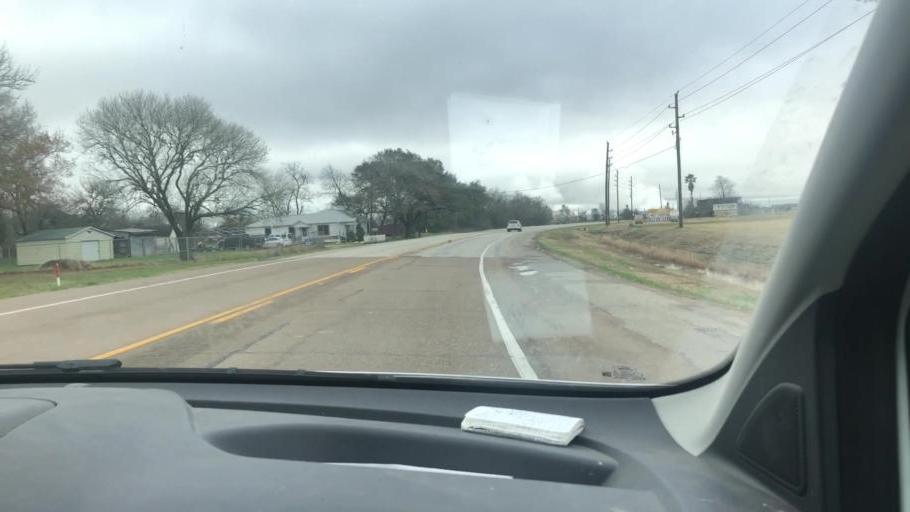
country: US
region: Texas
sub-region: Wharton County
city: Wharton
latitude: 29.3052
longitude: -96.0819
